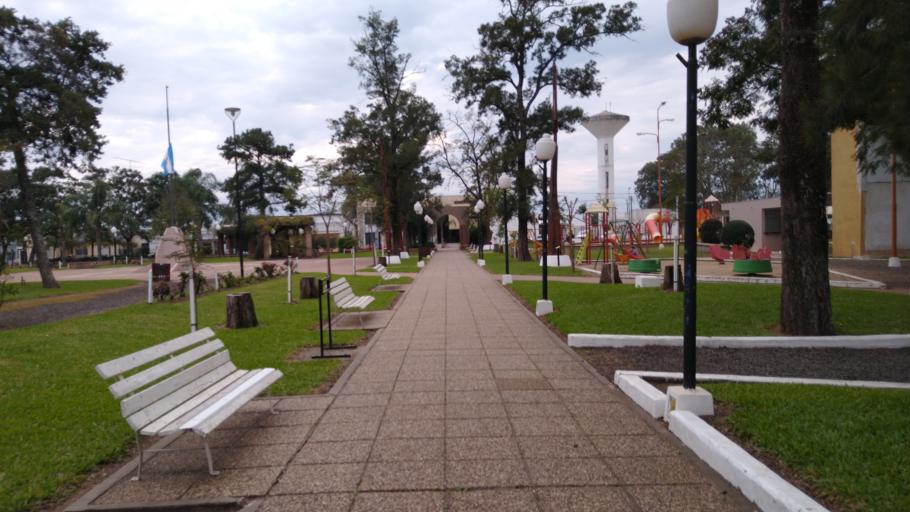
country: AR
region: Entre Rios
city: Villa del Rosario
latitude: -30.7961
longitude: -57.9148
